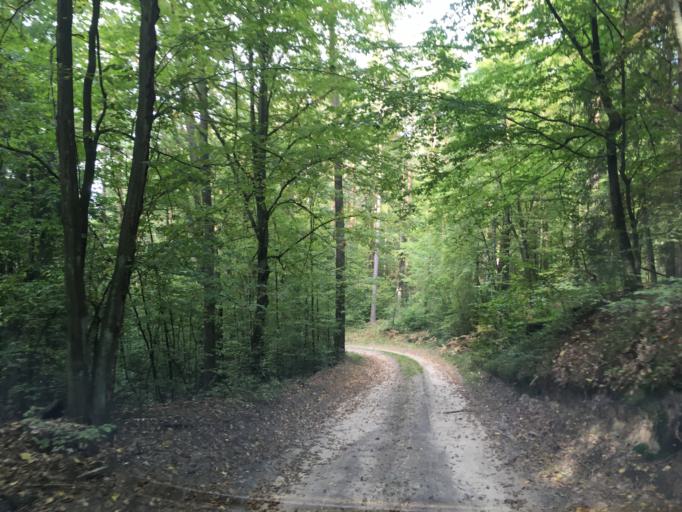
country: PL
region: Kujawsko-Pomorskie
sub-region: Powiat brodnicki
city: Gorzno
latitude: 53.2216
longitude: 19.7063
